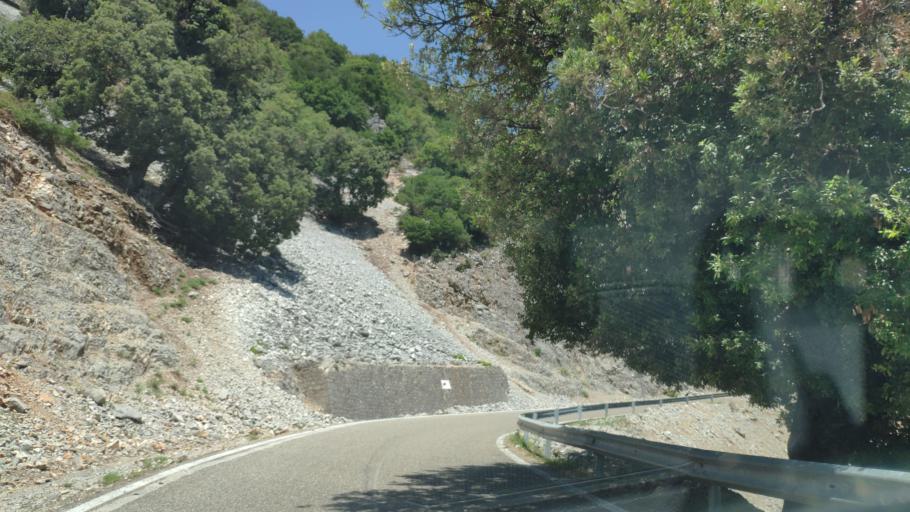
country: GR
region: West Greece
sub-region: Nomos Aitolias kai Akarnanias
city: Krikellos
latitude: 39.0216
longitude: 21.3699
